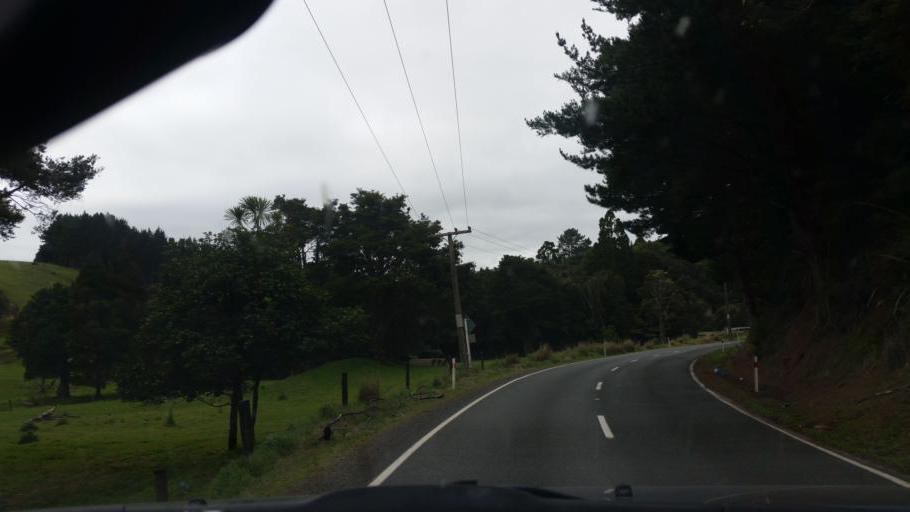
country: NZ
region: Northland
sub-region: Kaipara District
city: Dargaville
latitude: -35.8110
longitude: 173.7273
